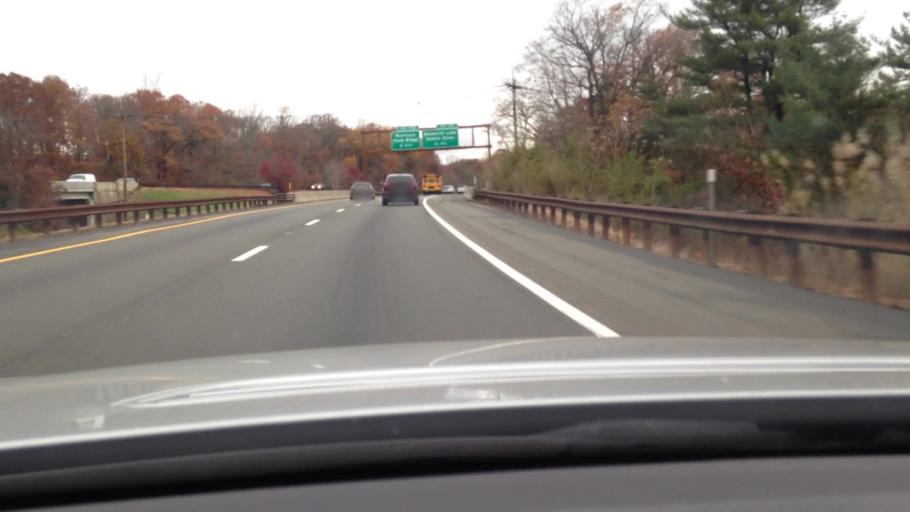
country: US
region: New Jersey
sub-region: Bergen County
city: Woodcliff Lake
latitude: 41.0238
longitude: -74.0697
